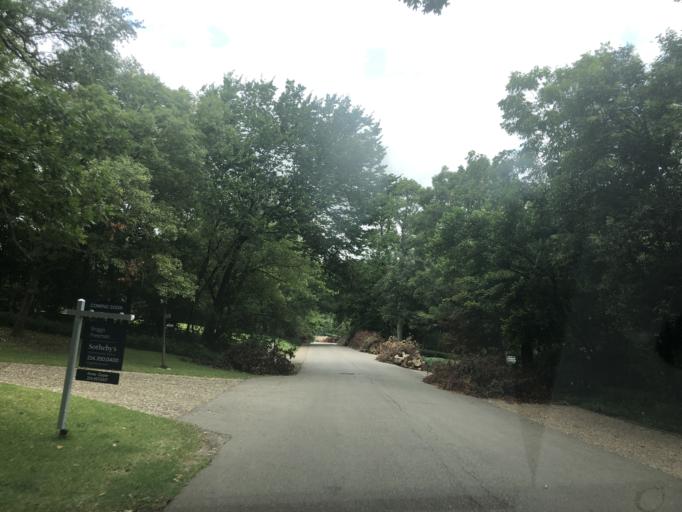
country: US
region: Texas
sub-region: Dallas County
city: University Park
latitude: 32.8595
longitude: -96.8279
